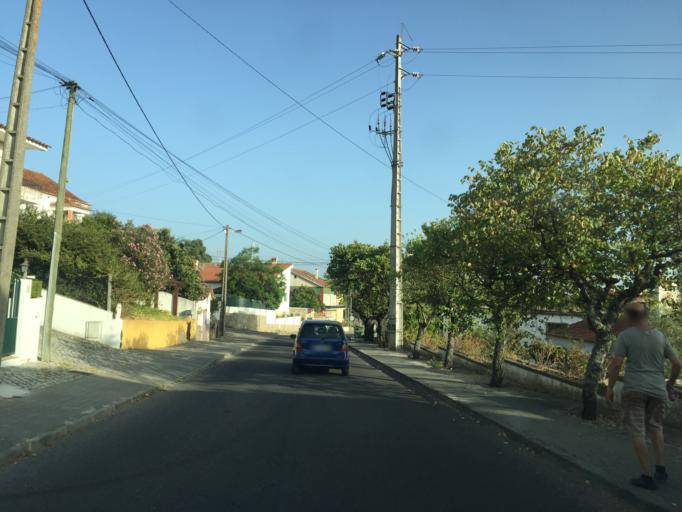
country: PT
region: Santarem
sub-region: Chamusca
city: Vila Nova da Barquinha
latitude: 39.4635
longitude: -8.4375
